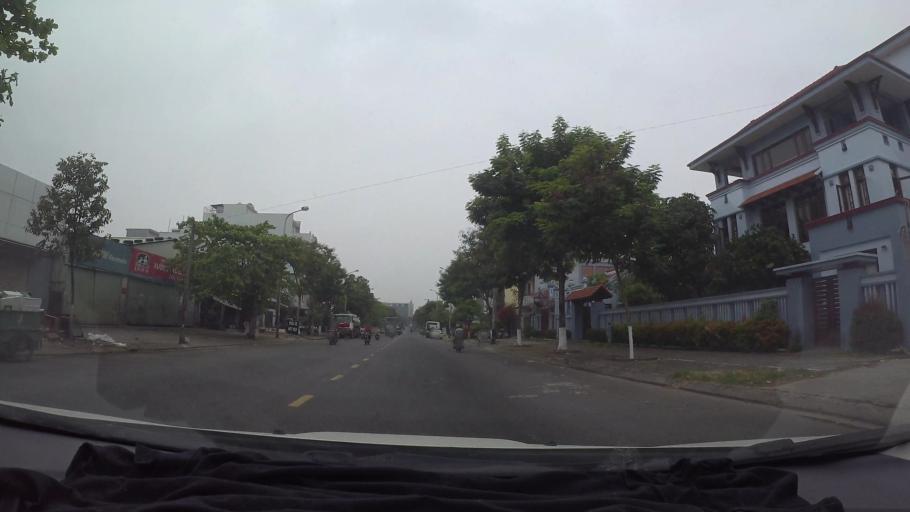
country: VN
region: Da Nang
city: Cam Le
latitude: 16.0270
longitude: 108.2138
